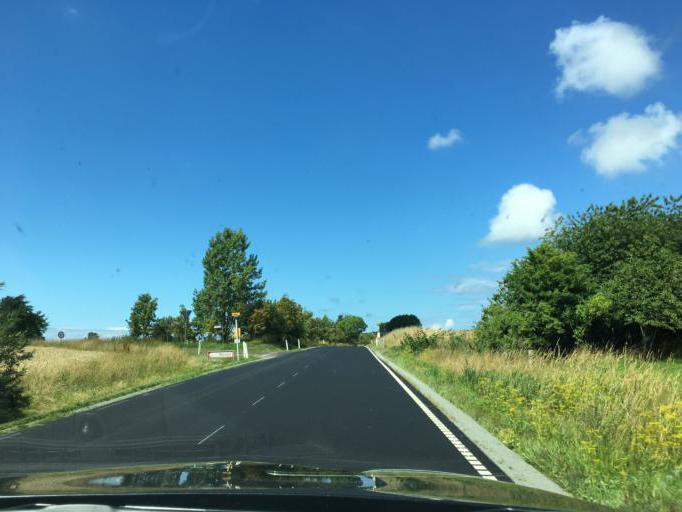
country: DK
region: Capital Region
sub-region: Gribskov Kommune
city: Helsinge
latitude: 56.0667
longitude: 12.2010
